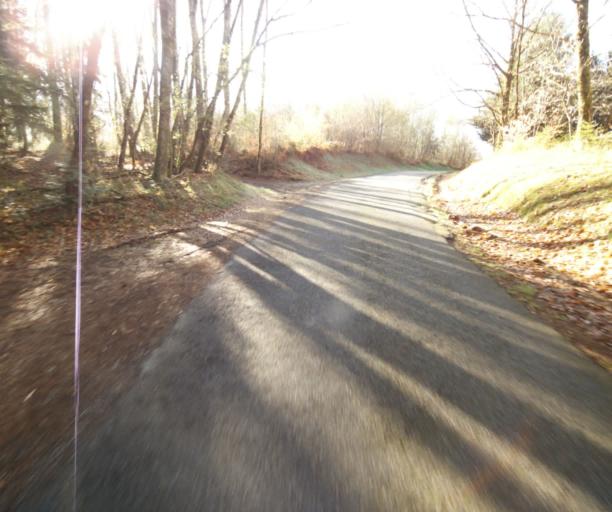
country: FR
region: Limousin
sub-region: Departement de la Correze
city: Laguenne
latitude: 45.2764
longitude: 1.8628
